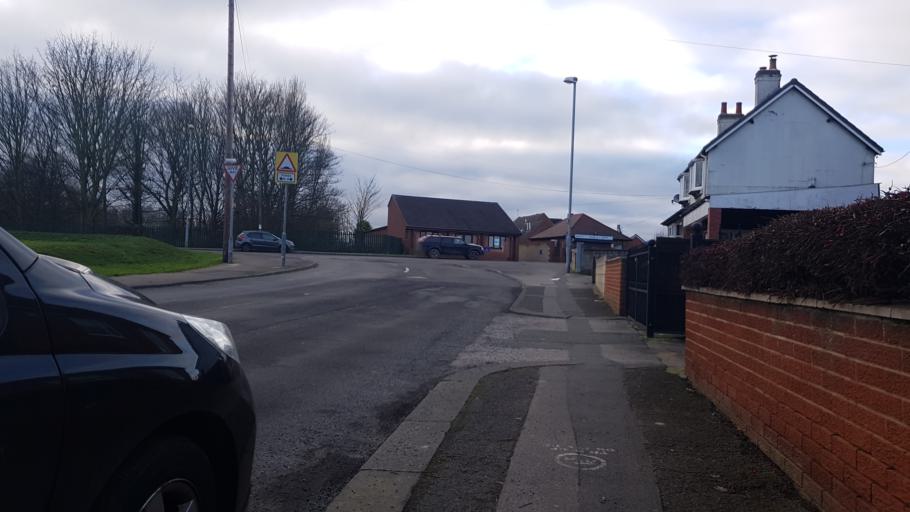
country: GB
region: England
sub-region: City and Borough of Wakefield
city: Pontefract
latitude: 53.7198
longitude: -1.3260
